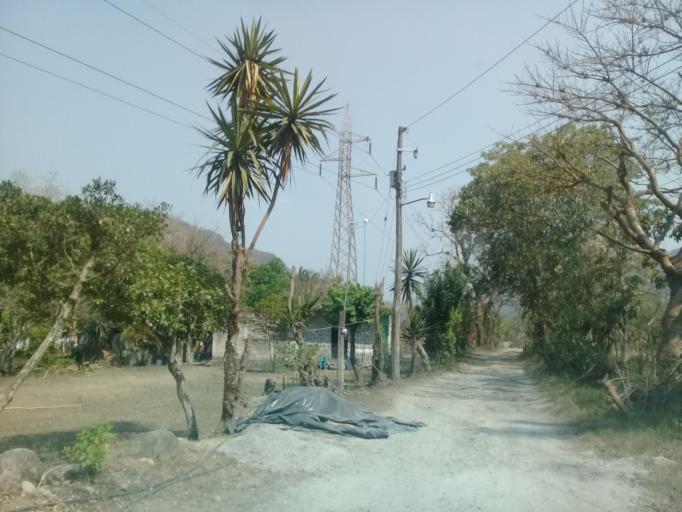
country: MX
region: Veracruz
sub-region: Ixtaczoquitlan
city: Campo Chico
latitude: 18.8318
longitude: -97.0233
